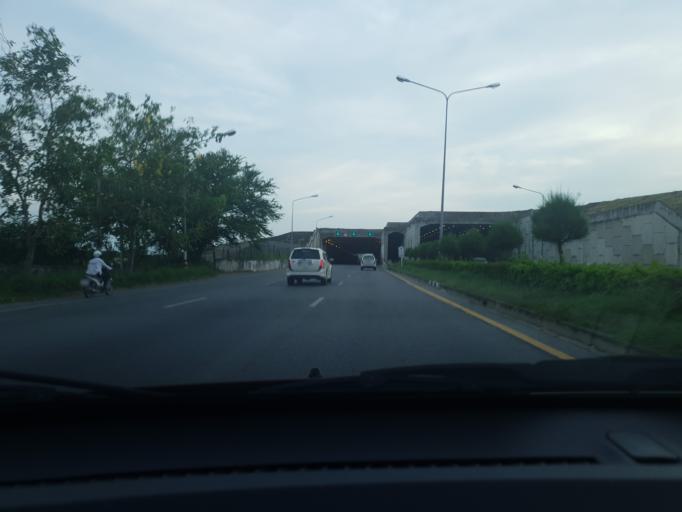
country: TH
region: Prachuap Khiri Khan
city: Hua Hin
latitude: 12.6442
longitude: 99.9491
